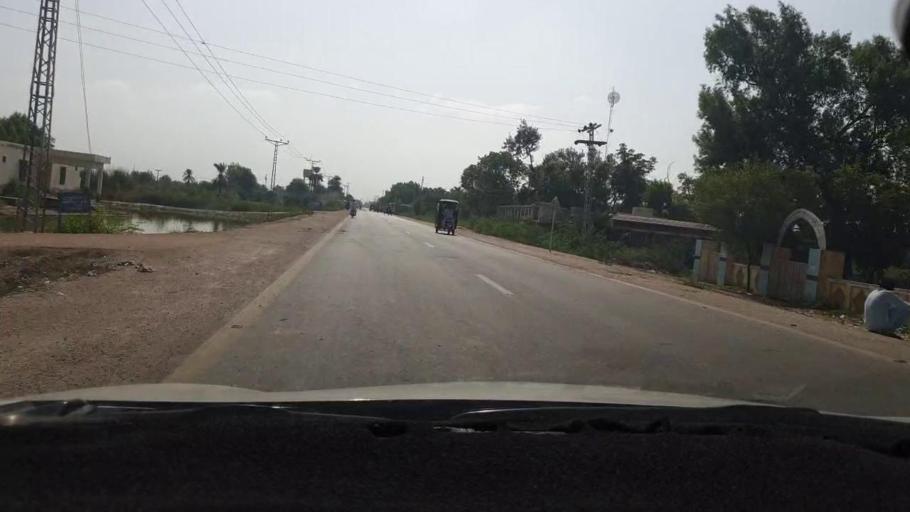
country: PK
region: Sindh
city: Mirpur Khas
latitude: 25.7229
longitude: 69.1138
